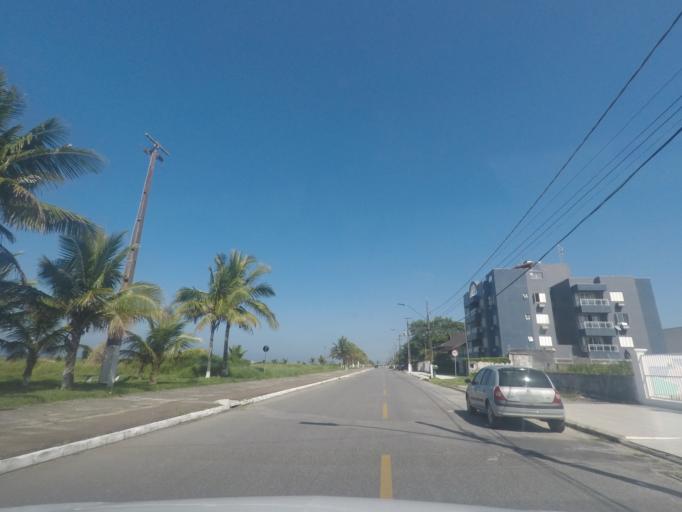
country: BR
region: Parana
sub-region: Pontal Do Parana
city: Pontal do Parana
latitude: -25.7226
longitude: -48.4838
